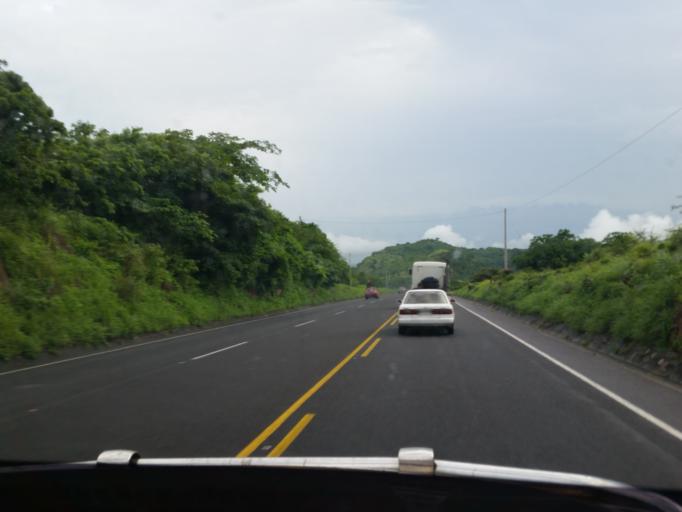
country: NI
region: Matagalpa
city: Ciudad Dario
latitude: 12.5174
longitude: -86.0527
